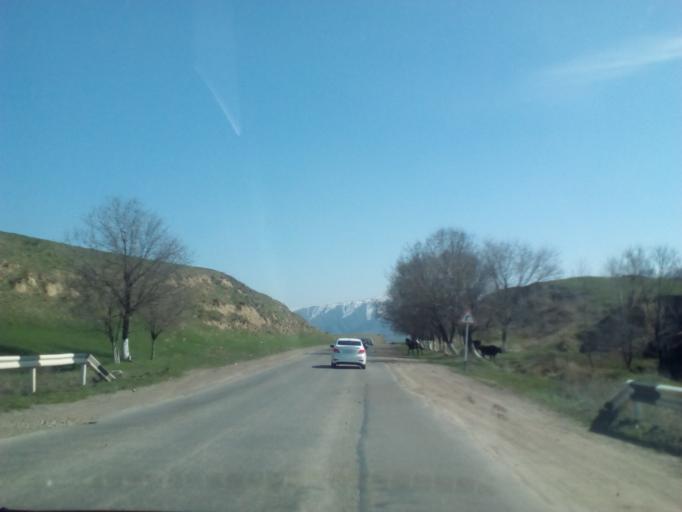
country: KZ
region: Almaty Oblysy
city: Burunday
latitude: 43.1776
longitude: 76.4289
